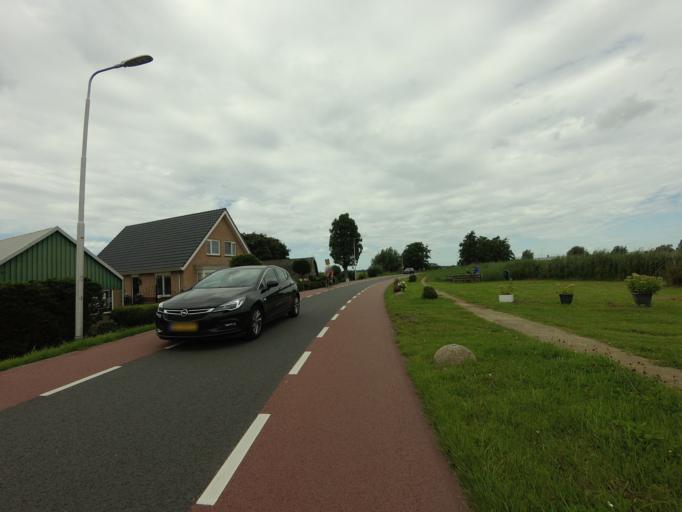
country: NL
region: North Holland
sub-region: Gemeente Uithoorn
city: Uithoorn
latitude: 52.2474
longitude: 4.8565
